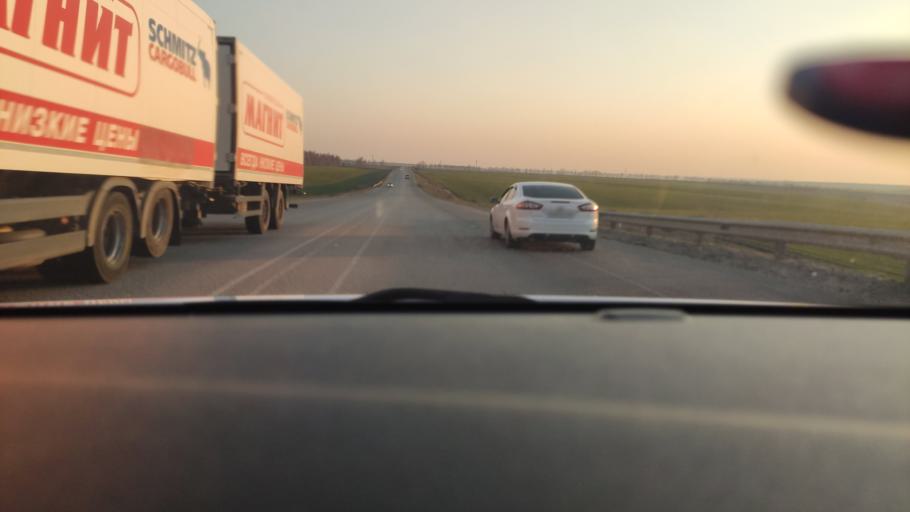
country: RU
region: Voronezj
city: Kolodeznyy
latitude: 51.4056
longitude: 39.2429
